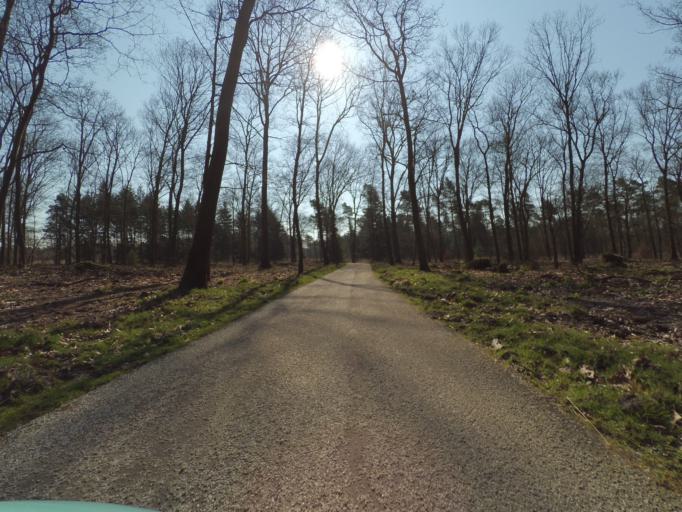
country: NL
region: Gelderland
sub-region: Gemeente Ede
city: Otterlo
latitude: 52.1168
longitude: 5.8465
